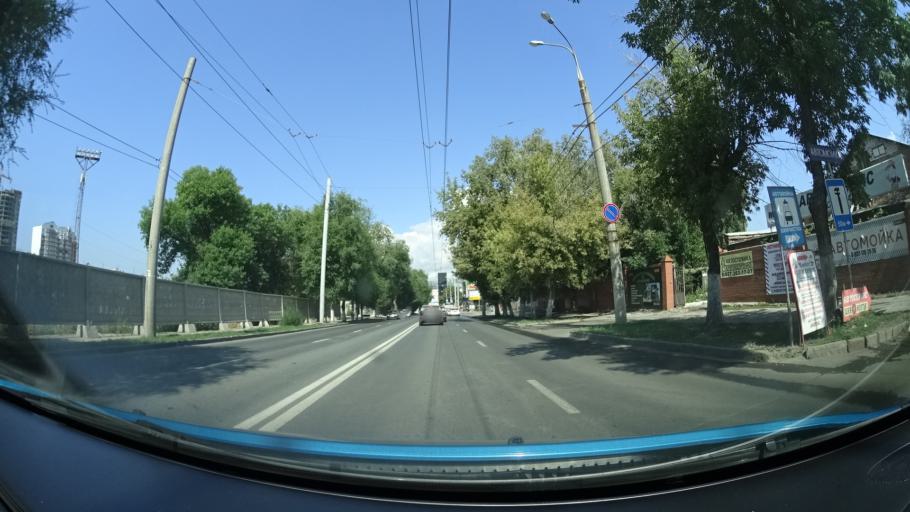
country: RU
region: Samara
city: Samara
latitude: 53.2143
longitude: 50.1519
